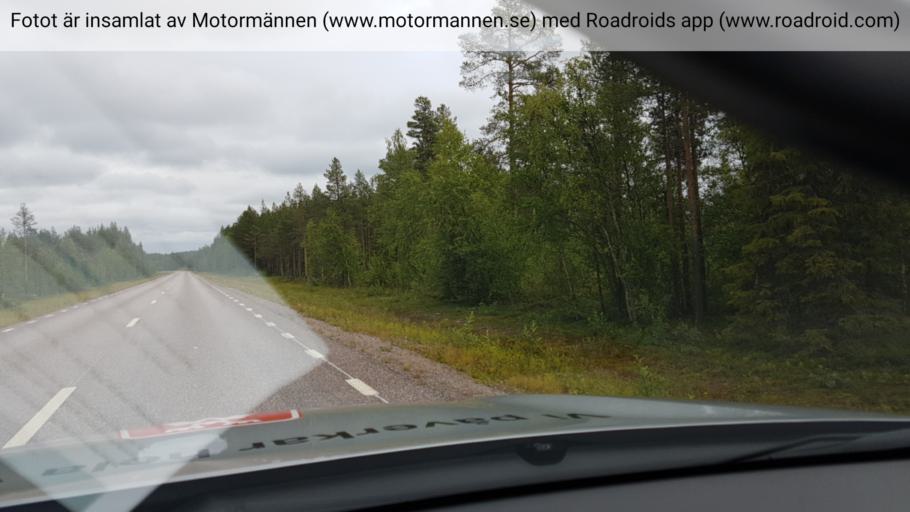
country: SE
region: Norrbotten
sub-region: Gallivare Kommun
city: Gaellivare
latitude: 67.0577
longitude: 21.2524
